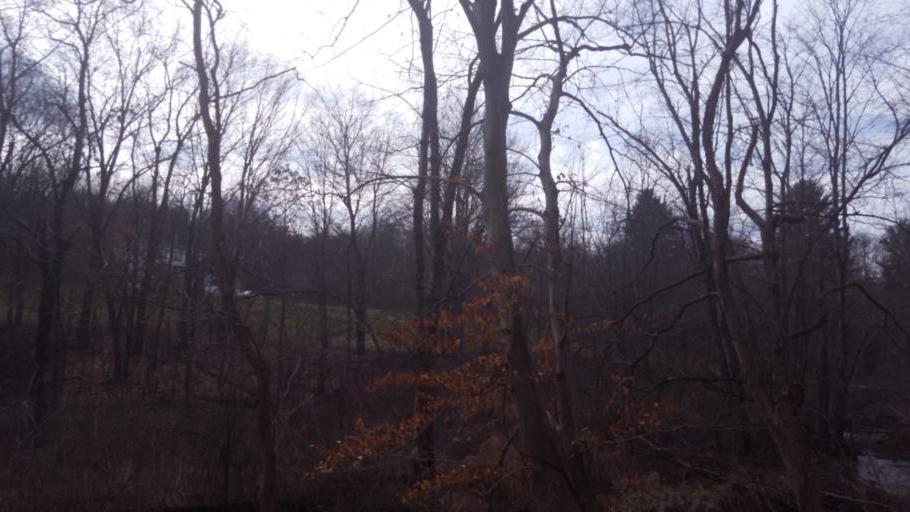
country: US
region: Ohio
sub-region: Knox County
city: Mount Vernon
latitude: 40.4457
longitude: -82.4337
